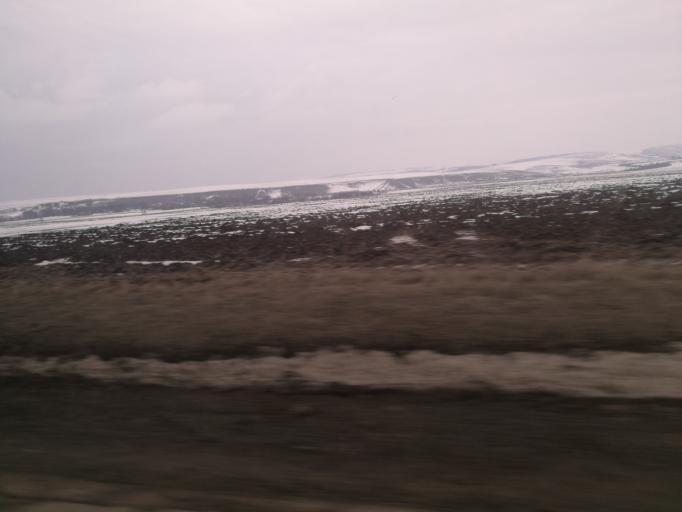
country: RO
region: Iasi
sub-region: Comuna Ruginoasa
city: Dumbravita
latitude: 47.2348
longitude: 26.8169
